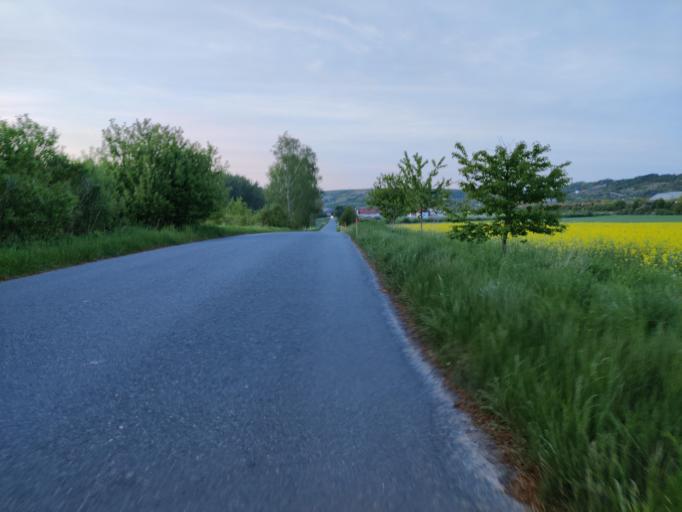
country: DE
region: Saxony-Anhalt
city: Karsdorf
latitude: 51.2678
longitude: 11.6487
